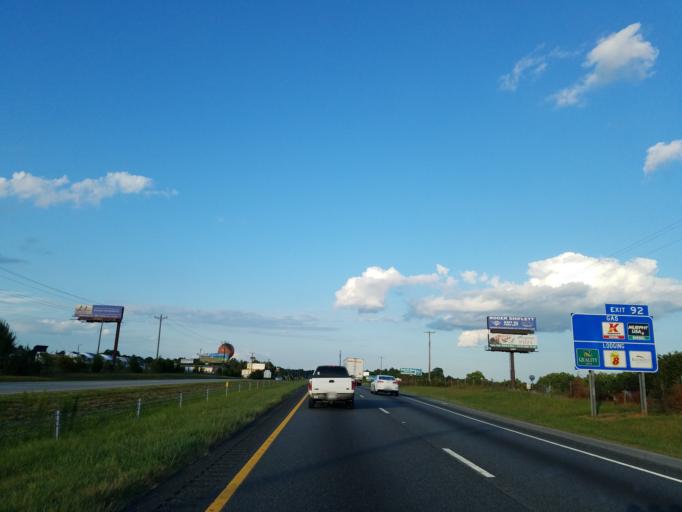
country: US
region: South Carolina
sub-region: Cherokee County
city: Gaffney
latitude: 35.0904
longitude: -81.6920
